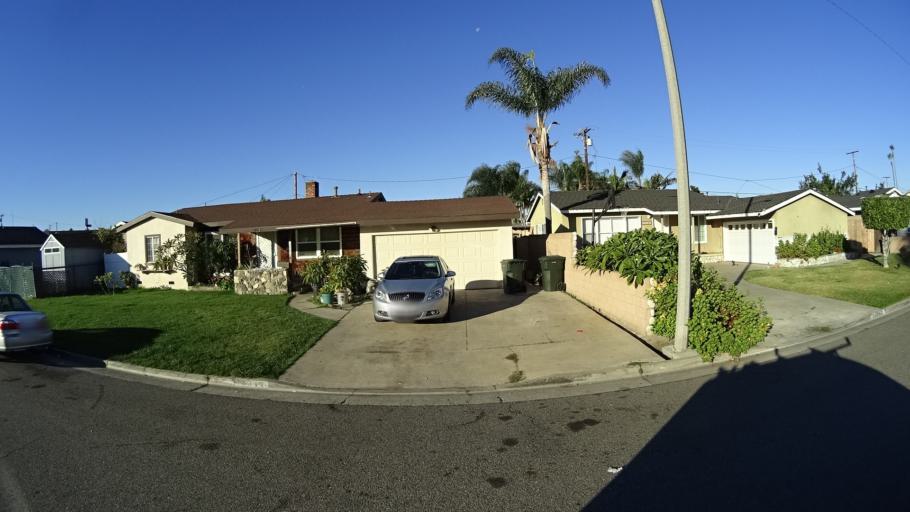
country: US
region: California
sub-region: Orange County
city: Midway City
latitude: 33.7684
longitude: -117.9750
